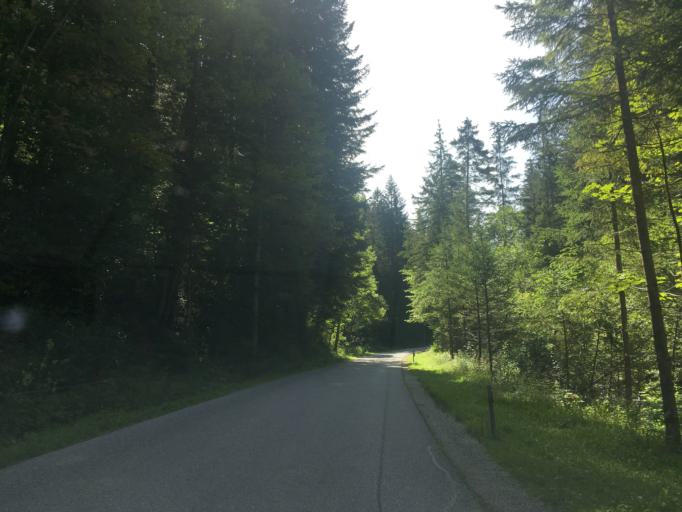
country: AT
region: Salzburg
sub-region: Politischer Bezirk Hallein
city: Abtenau
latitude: 47.5216
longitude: 13.4468
